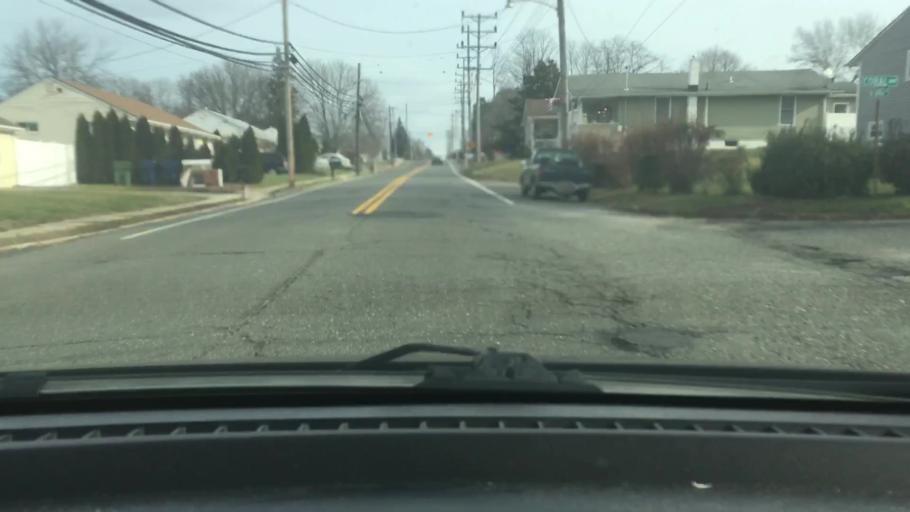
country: US
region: New Jersey
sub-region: Monmouth County
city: Shark River Hills
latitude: 40.2167
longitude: -74.0711
